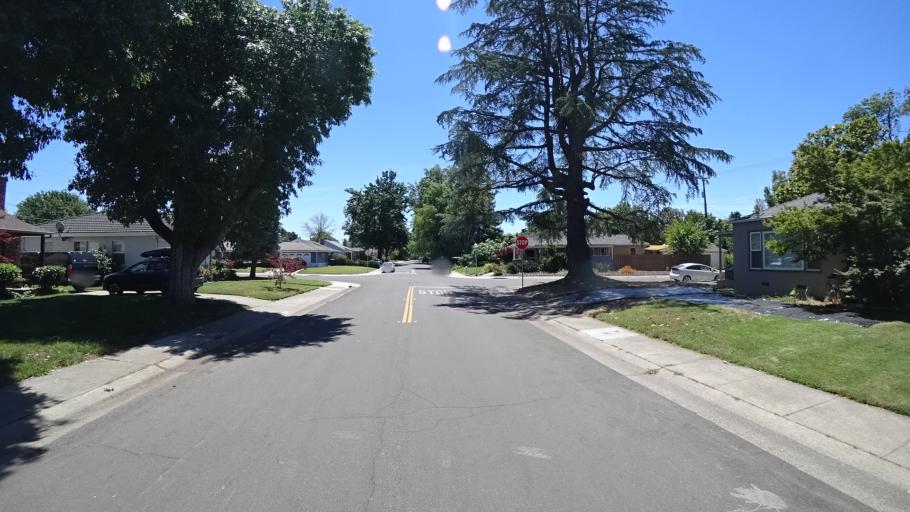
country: US
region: California
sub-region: Sacramento County
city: Sacramento
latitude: 38.5799
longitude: -121.4499
